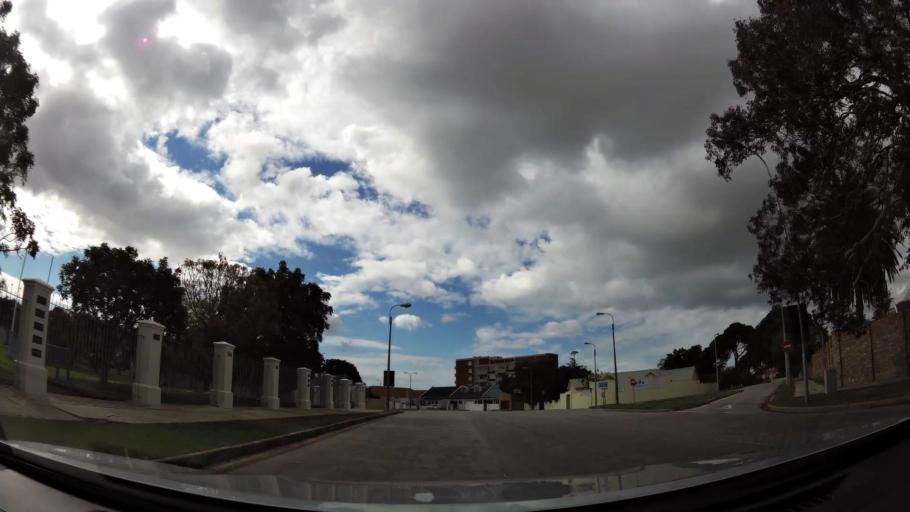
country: ZA
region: Eastern Cape
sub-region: Nelson Mandela Bay Metropolitan Municipality
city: Port Elizabeth
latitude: -33.9614
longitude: 25.5989
